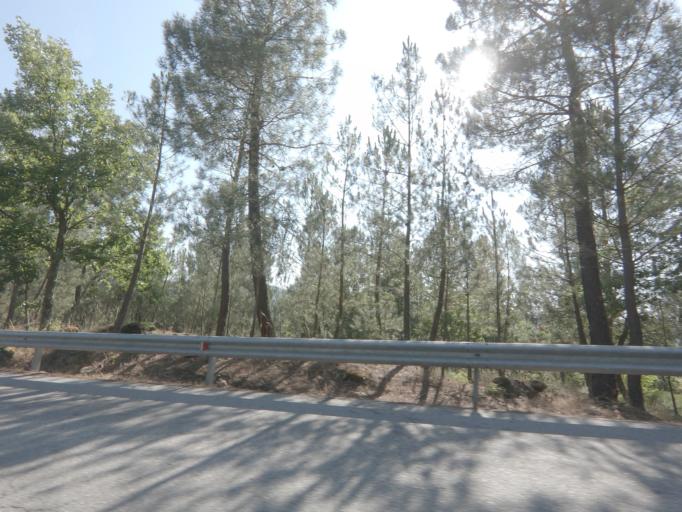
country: PT
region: Viseu
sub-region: Moimenta da Beira
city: Moimenta da Beira
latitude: 40.9762
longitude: -7.5782
